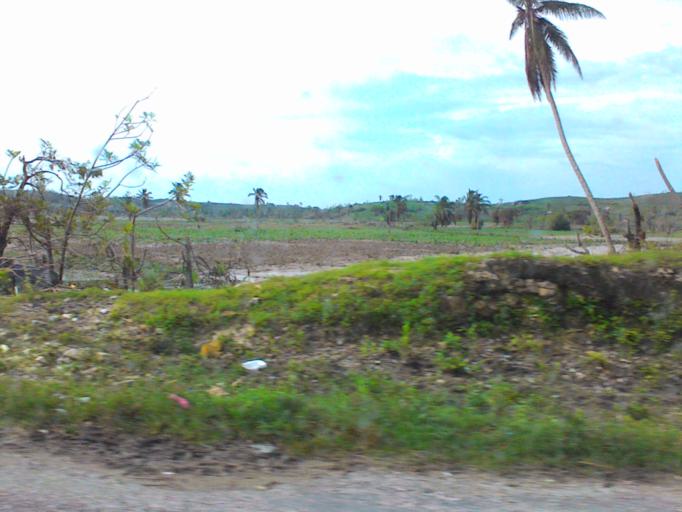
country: HT
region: Sud
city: Les Cayes
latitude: 18.2487
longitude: -73.7438
